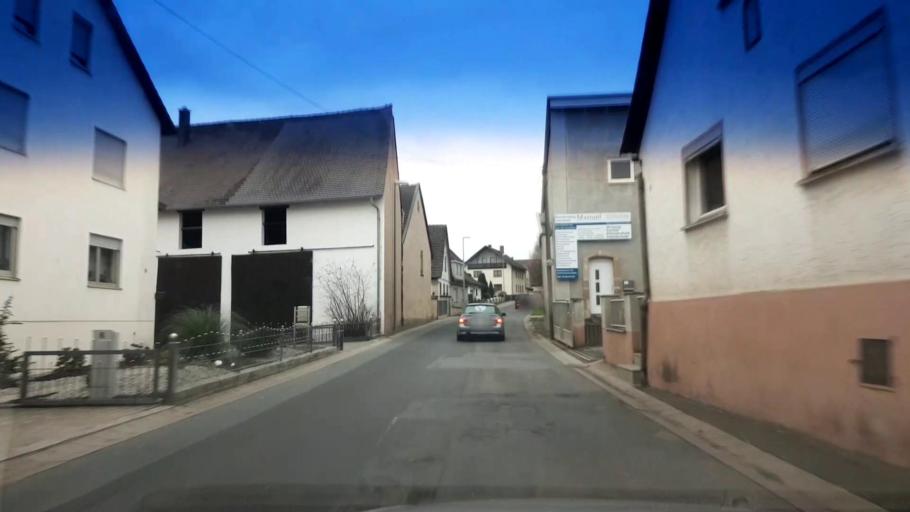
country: DE
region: Bavaria
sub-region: Upper Franconia
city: Pettstadt
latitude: 49.7994
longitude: 10.9226
